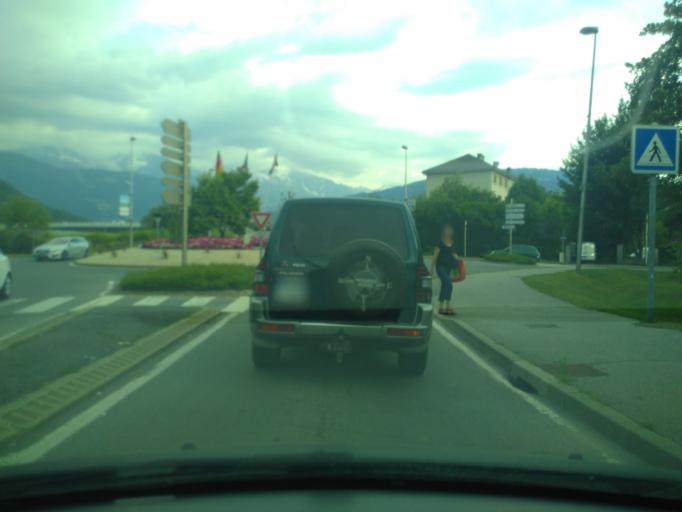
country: FR
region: Rhone-Alpes
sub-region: Departement de la Haute-Savoie
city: Sallanches
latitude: 45.9399
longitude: 6.6401
